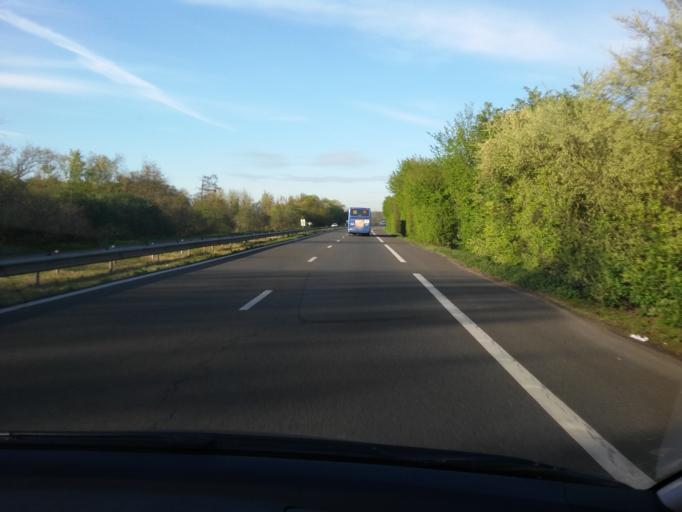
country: FR
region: Picardie
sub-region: Departement de l'Oise
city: Lacroix-Saint-Ouen
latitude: 49.3685
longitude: 2.7770
